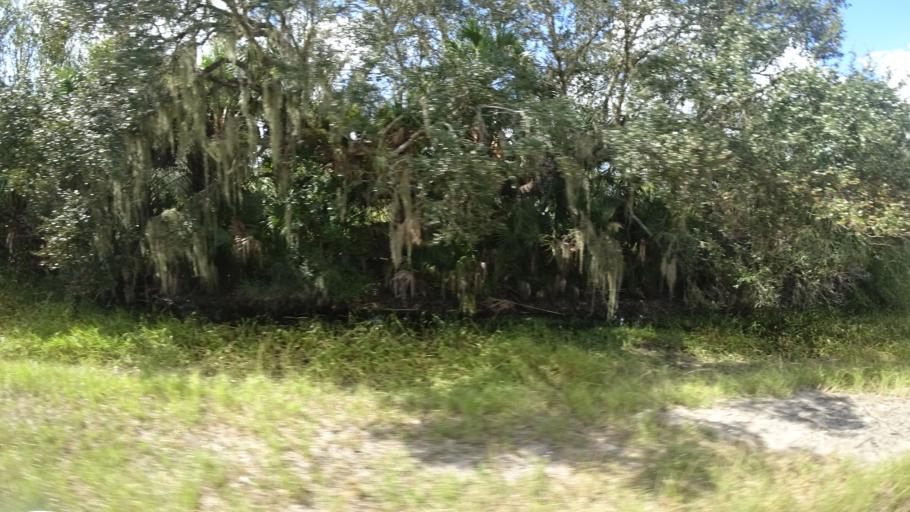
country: US
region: Florida
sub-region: Sarasota County
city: North Port
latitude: 27.2403
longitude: -82.1219
